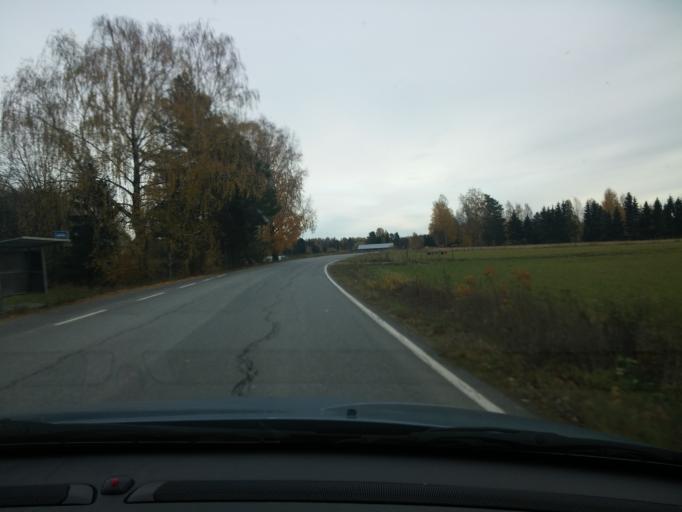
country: FI
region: Haeme
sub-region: Forssa
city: Tammela
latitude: 60.7671
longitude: 23.8496
